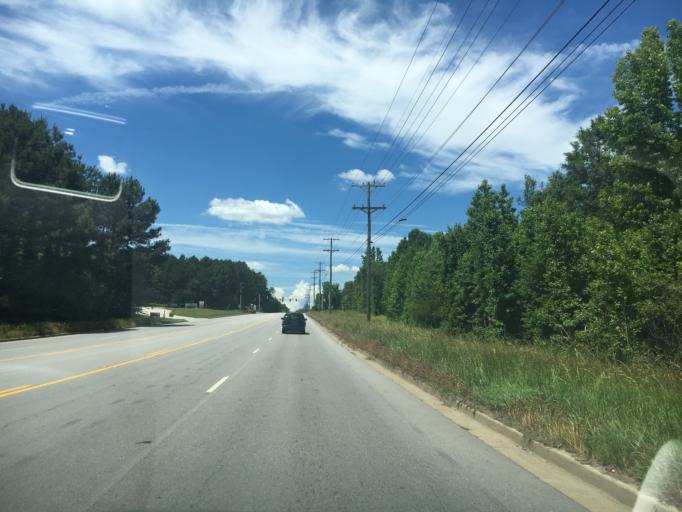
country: US
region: South Carolina
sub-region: Spartanburg County
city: Duncan
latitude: 34.8733
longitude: -82.1442
